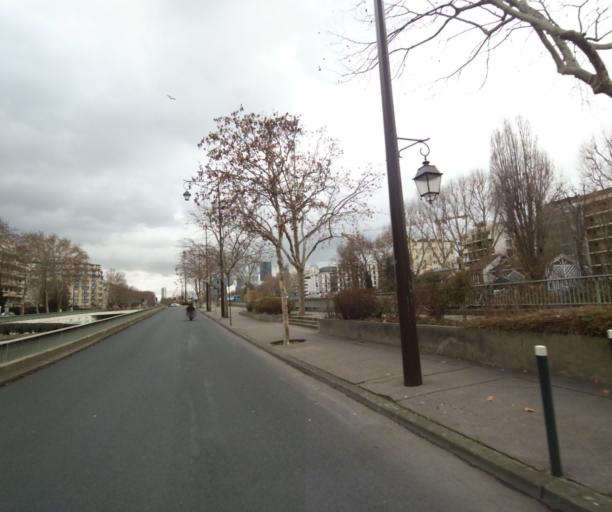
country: FR
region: Ile-de-France
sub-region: Departement des Hauts-de-Seine
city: Neuilly-sur-Seine
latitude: 48.8946
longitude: 2.2692
